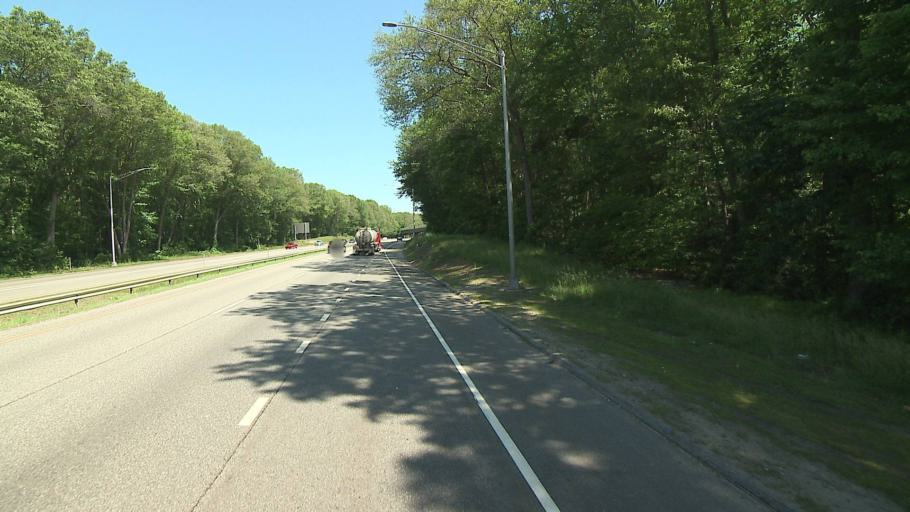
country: US
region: Connecticut
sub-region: New London County
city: Norwich
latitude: 41.5146
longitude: -72.1189
